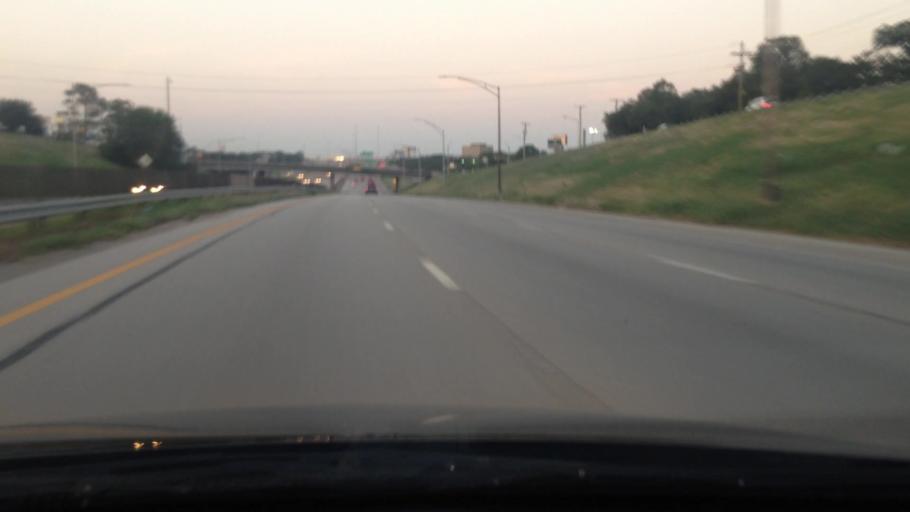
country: US
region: Texas
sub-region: Tarrant County
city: Haltom City
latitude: 32.7439
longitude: -97.2236
